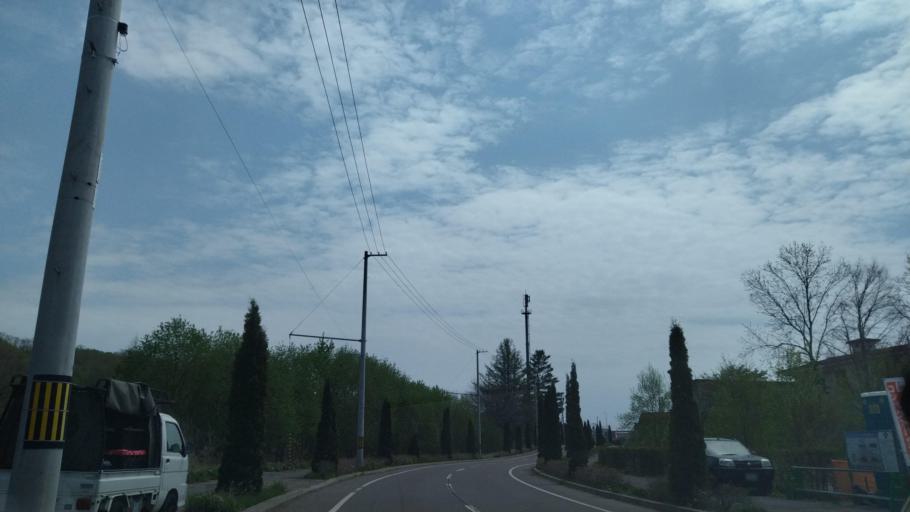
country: JP
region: Hokkaido
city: Otofuke
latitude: 43.2513
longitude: 143.5498
